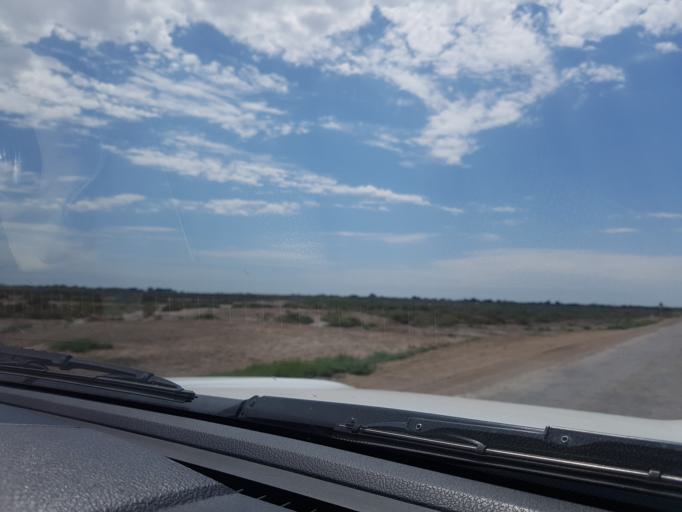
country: TM
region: Dasoguz
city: Koeneuergench
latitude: 42.3049
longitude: 59.1368
